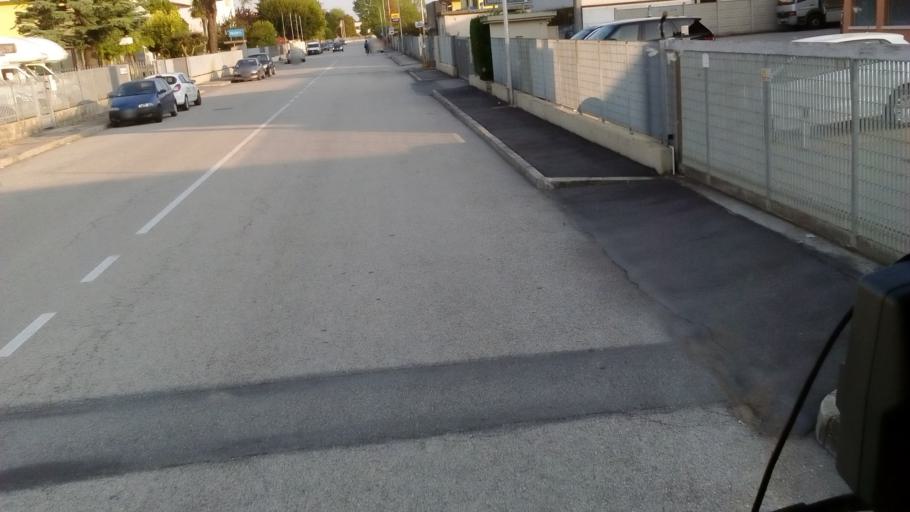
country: IT
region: Veneto
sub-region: Provincia di Padova
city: Villatora
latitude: 45.3832
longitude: 11.9610
